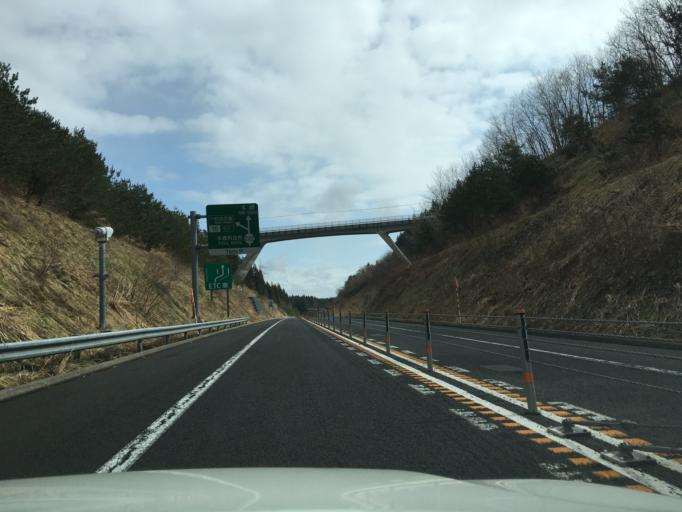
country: JP
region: Akita
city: Akita
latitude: 39.6314
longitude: 140.1678
